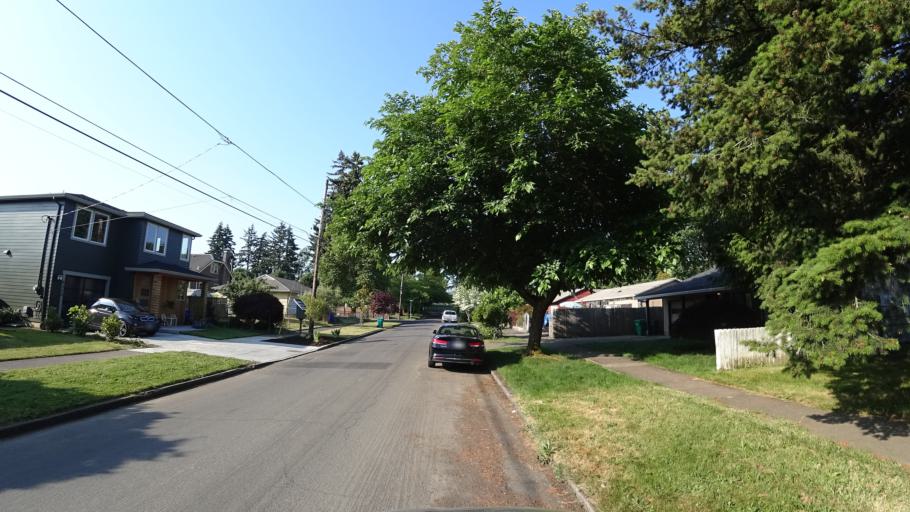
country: US
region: Oregon
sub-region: Washington County
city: West Haven
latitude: 45.5925
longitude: -122.7381
